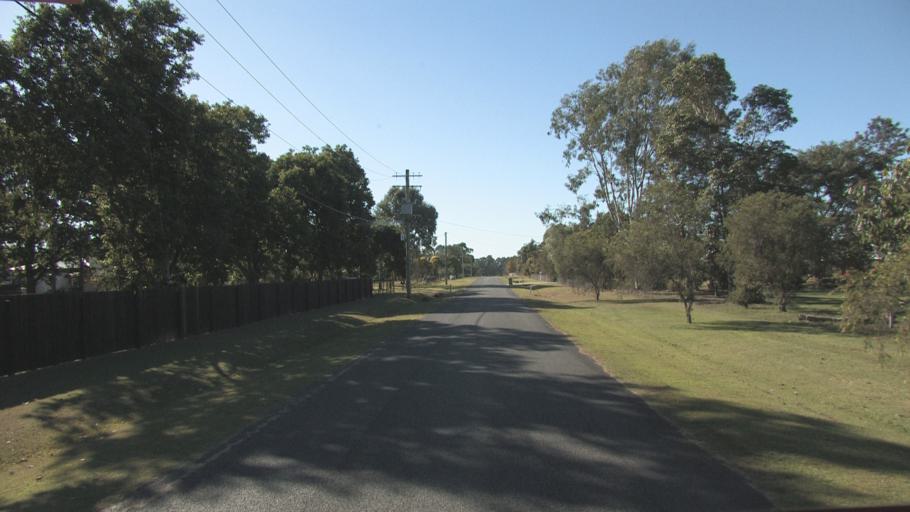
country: AU
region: Queensland
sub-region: Logan
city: Logan Reserve
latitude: -27.7410
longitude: 153.1131
